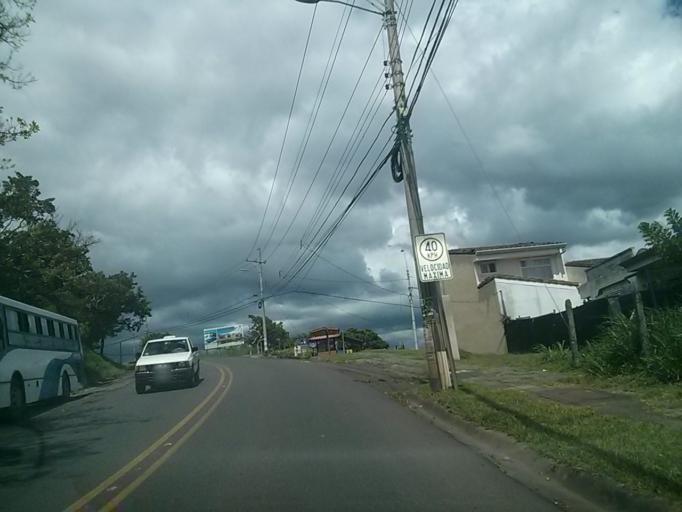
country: CR
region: Heredia
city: La Asuncion
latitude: 9.9623
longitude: -84.1739
